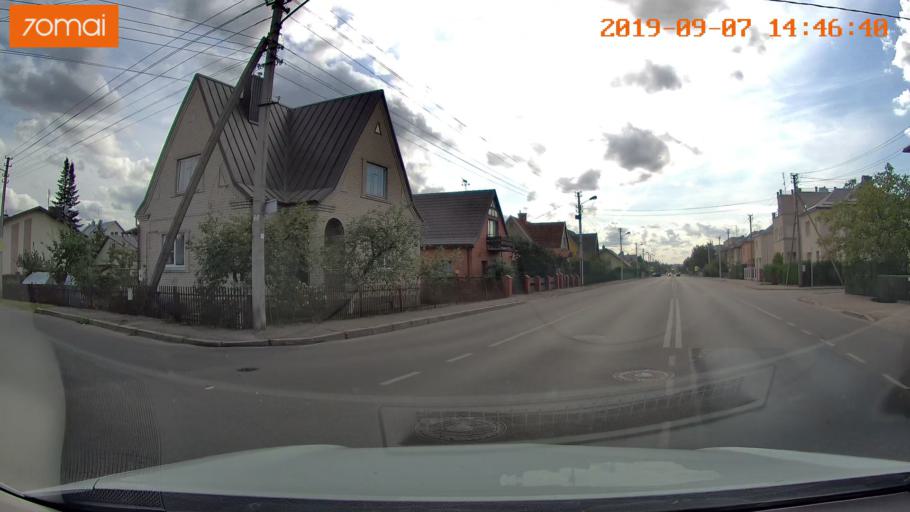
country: LT
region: Kauno apskritis
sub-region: Kaunas
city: Silainiai
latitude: 54.9243
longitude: 23.9026
